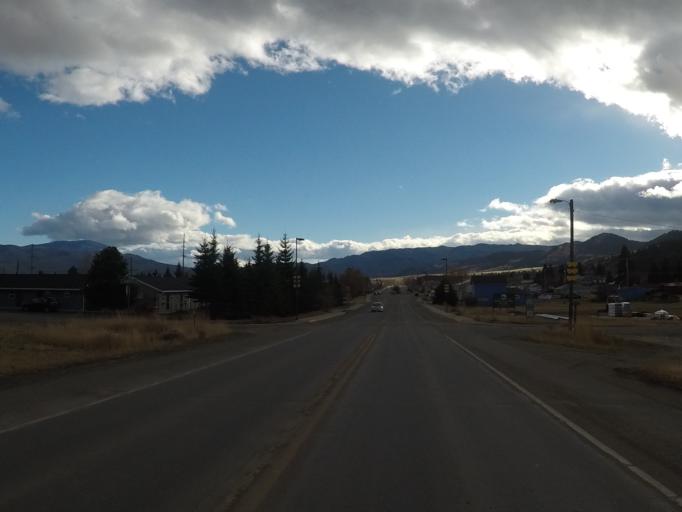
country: US
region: Montana
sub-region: Jefferson County
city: Boulder
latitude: 46.2410
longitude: -112.1175
